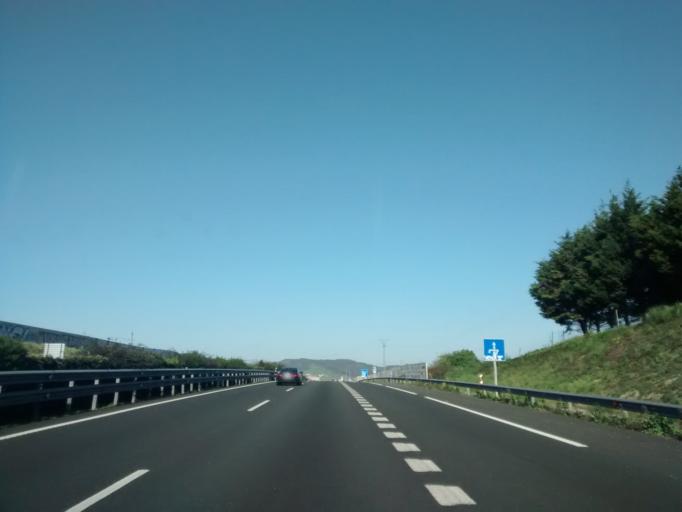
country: ES
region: Cantabria
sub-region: Provincia de Cantabria
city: Santa Cruz de Bezana
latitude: 43.4376
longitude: -3.8798
